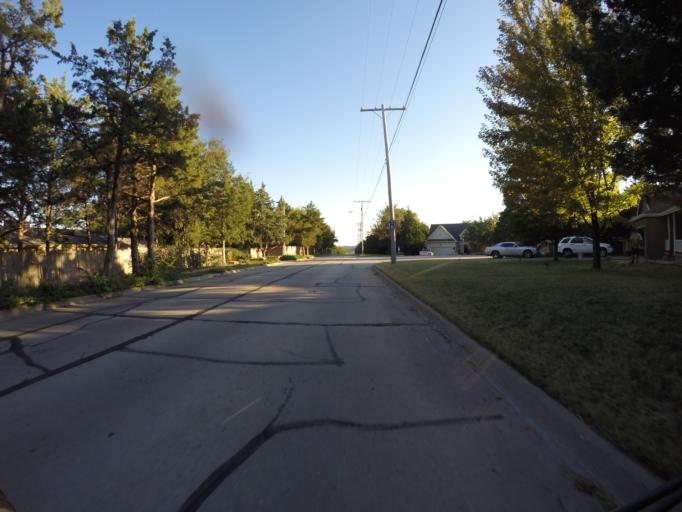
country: US
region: Kansas
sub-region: Riley County
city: Manhattan
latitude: 39.1994
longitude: -96.6261
